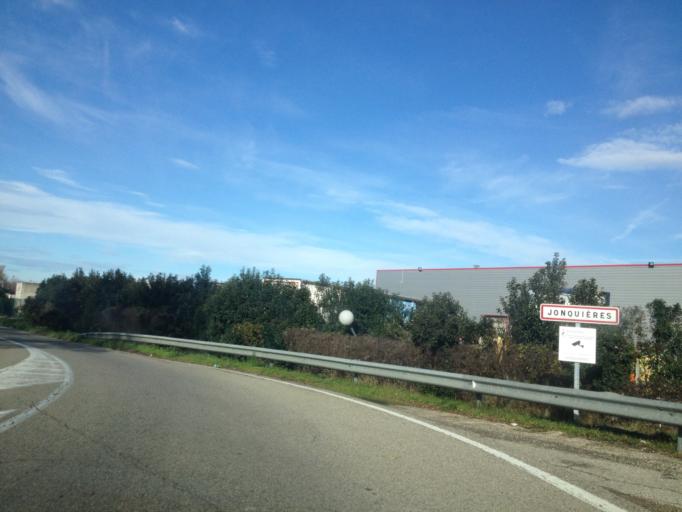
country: FR
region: Provence-Alpes-Cote d'Azur
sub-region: Departement du Vaucluse
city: Jonquieres
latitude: 44.1078
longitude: 4.9165
